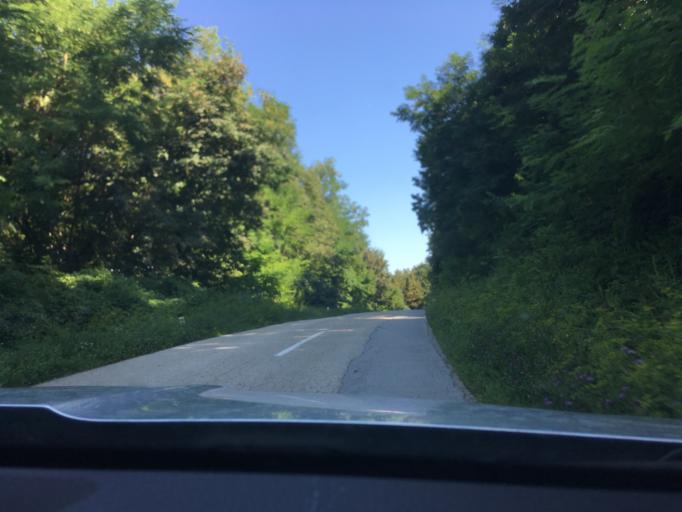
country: HR
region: Karlovacka
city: Ozalj
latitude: 45.4951
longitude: 15.3589
